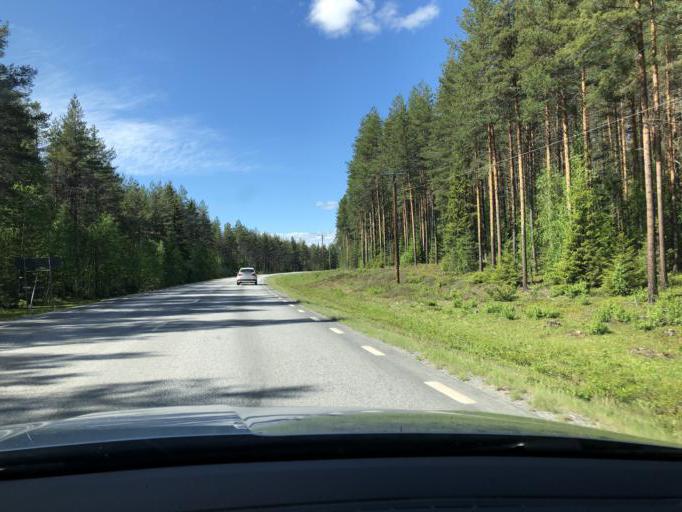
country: SE
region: Norrbotten
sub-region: Alvsbyns Kommun
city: AElvsbyn
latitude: 65.6499
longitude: 21.0909
